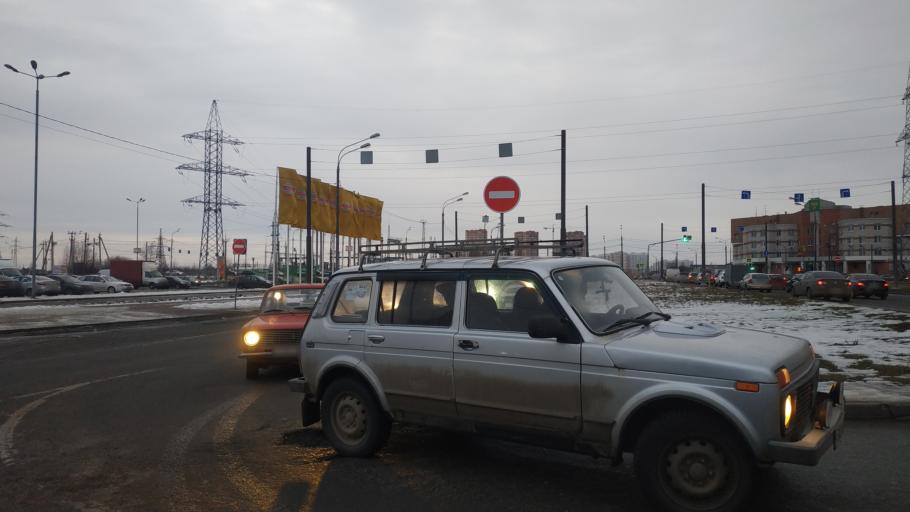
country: RU
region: Tverskaya
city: Tver
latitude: 56.8173
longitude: 35.8863
